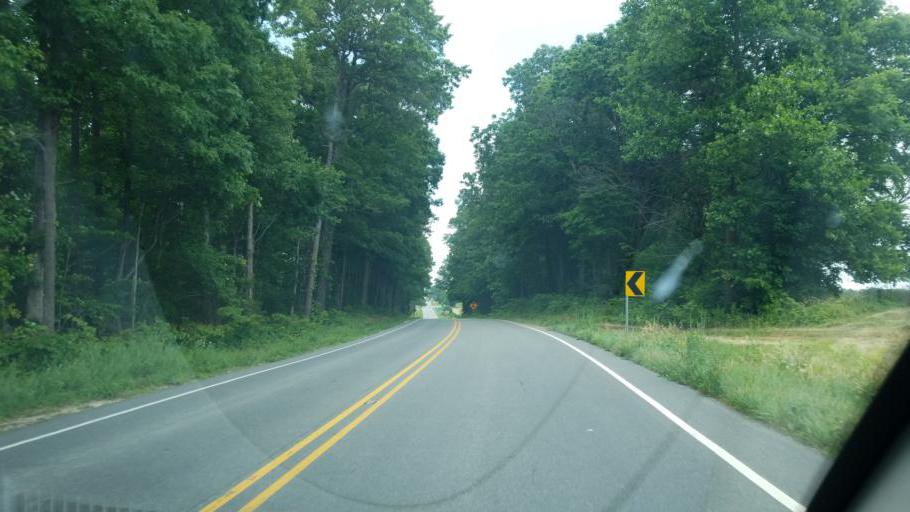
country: US
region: Virginia
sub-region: Buckingham County
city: Buckingham
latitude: 37.5343
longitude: -78.6210
